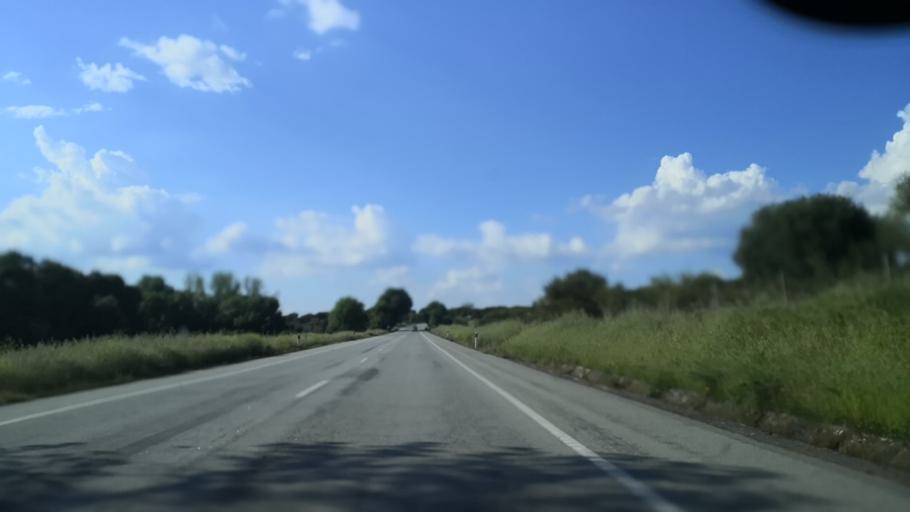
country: PT
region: Portalegre
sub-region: Portalegre
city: Urra
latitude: 39.0812
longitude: -7.4370
